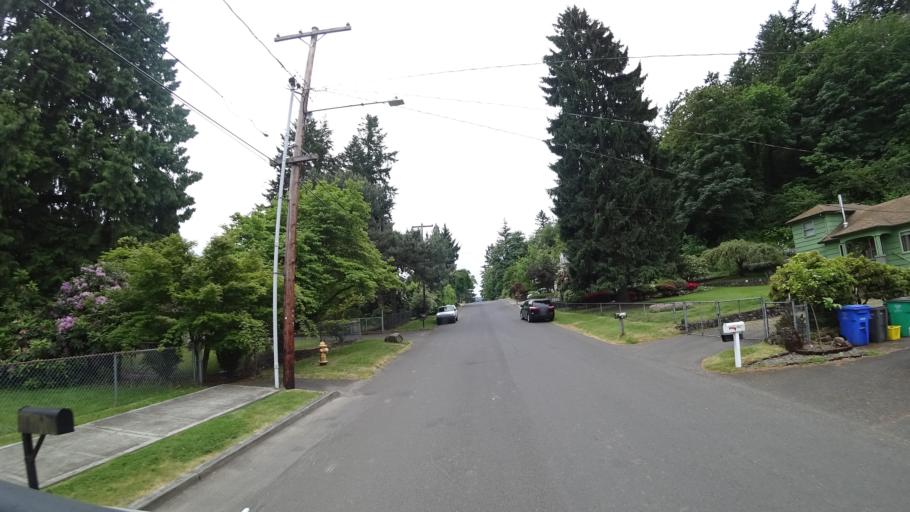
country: US
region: Oregon
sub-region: Multnomah County
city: Lents
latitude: 45.5015
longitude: -122.5514
